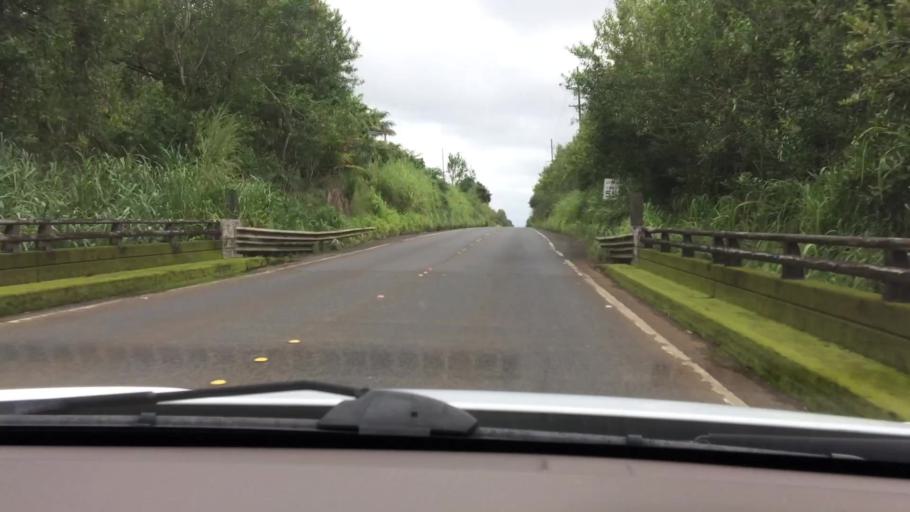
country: US
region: Hawaii
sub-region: Hawaii County
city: Pepeekeo
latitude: 19.8275
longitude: -155.1043
